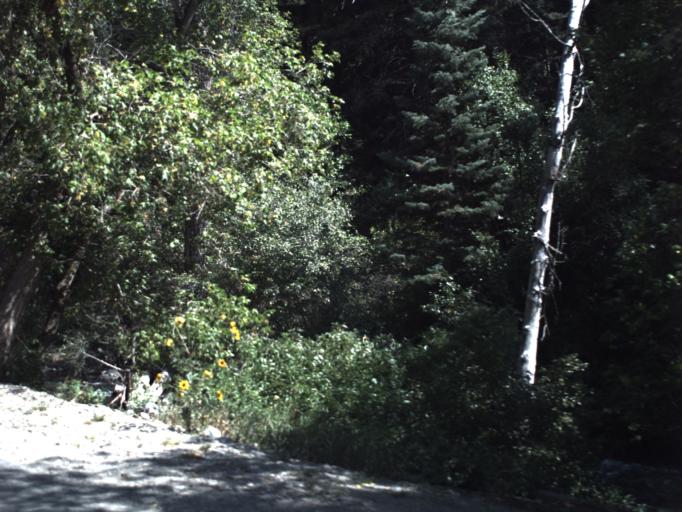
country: US
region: Utah
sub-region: Utah County
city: Highland
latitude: 40.4729
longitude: -111.6511
